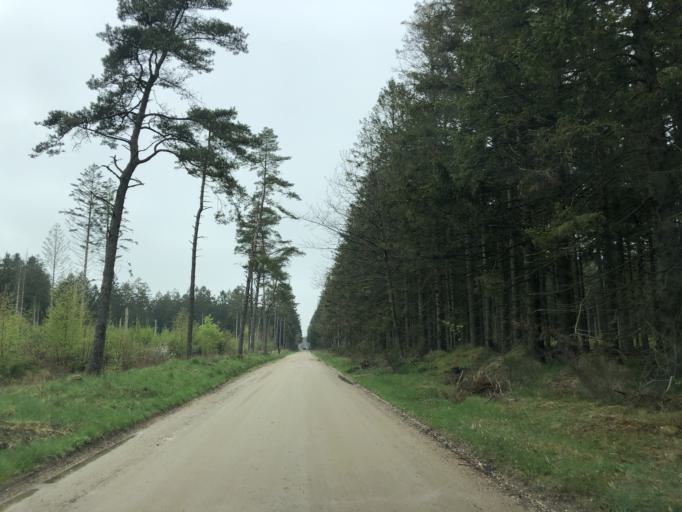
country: DK
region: Central Jutland
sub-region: Lemvig Kommune
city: Lemvig
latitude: 56.4986
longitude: 8.3365
